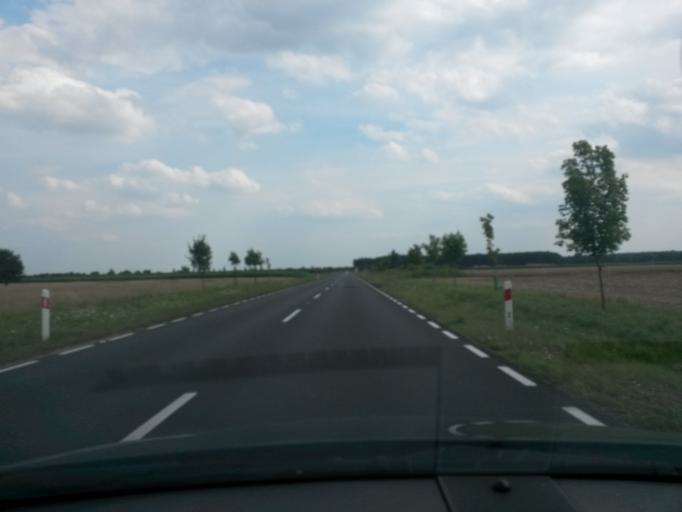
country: PL
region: Greater Poland Voivodeship
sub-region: Powiat poznanski
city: Kornik
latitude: 52.2305
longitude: 17.0664
